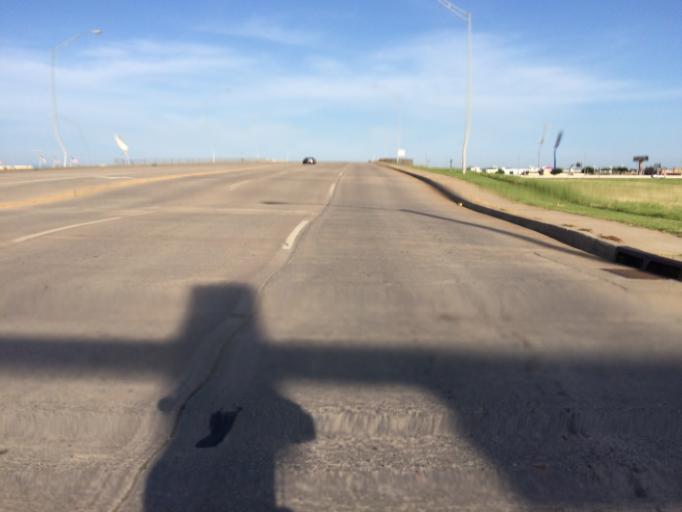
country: US
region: Oklahoma
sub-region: Cleveland County
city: Norman
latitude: 35.2330
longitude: -97.4830
